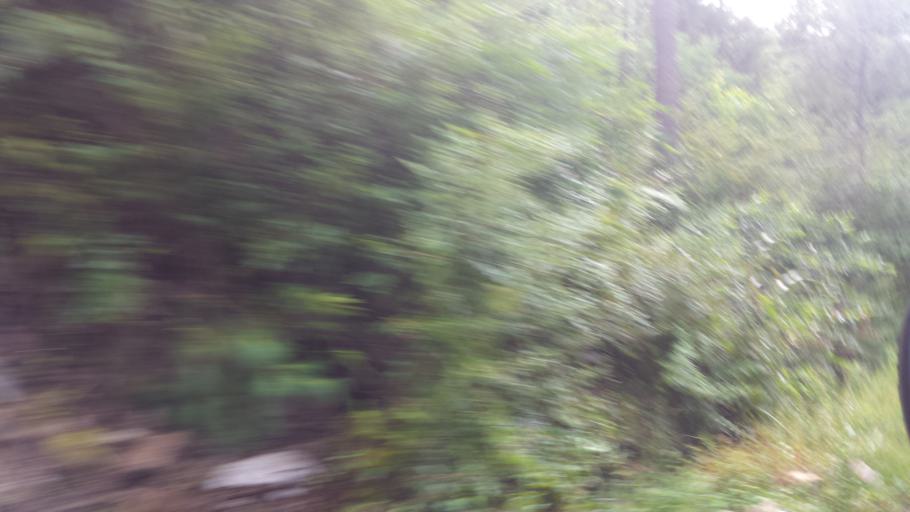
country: BT
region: Thimphu
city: Thimphu
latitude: 27.4036
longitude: 89.6584
